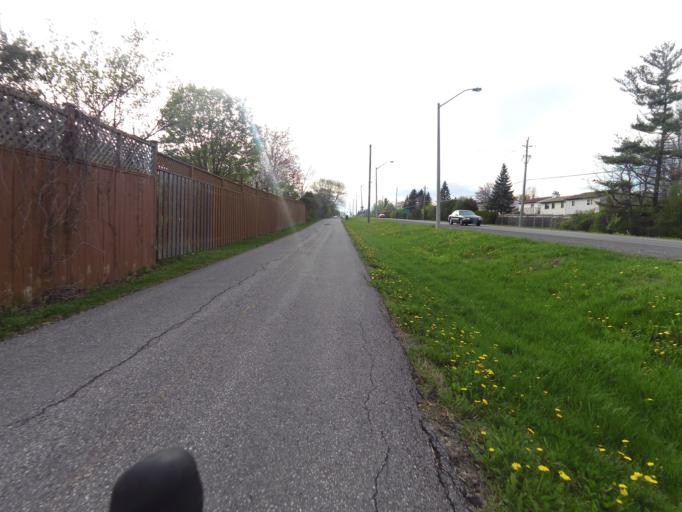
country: CA
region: Ontario
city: Bells Corners
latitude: 45.2727
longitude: -75.7612
